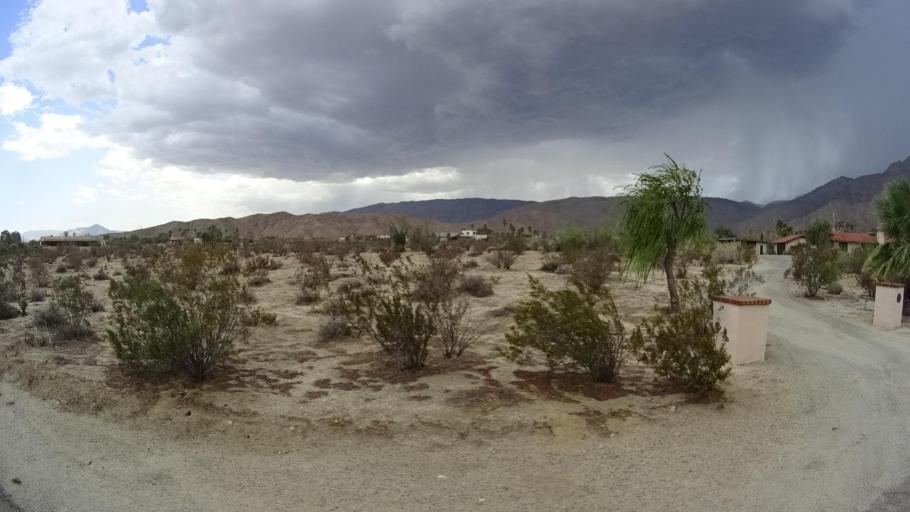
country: US
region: California
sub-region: San Diego County
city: Borrego Springs
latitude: 33.2649
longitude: -116.3949
